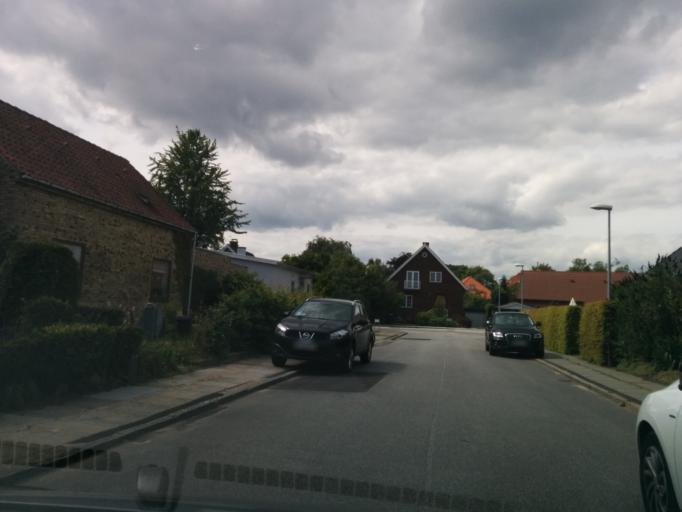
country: DK
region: Central Jutland
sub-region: Arhus Kommune
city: Arhus
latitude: 56.1357
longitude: 10.1851
